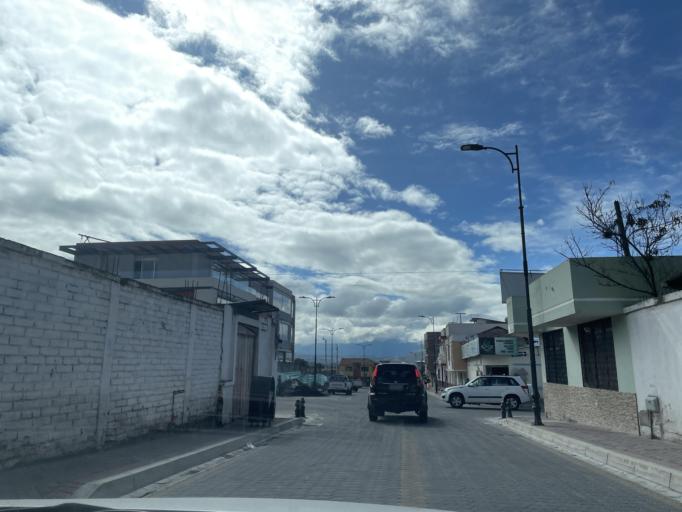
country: EC
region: Chimborazo
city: Guano
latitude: -1.6066
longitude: -78.6431
